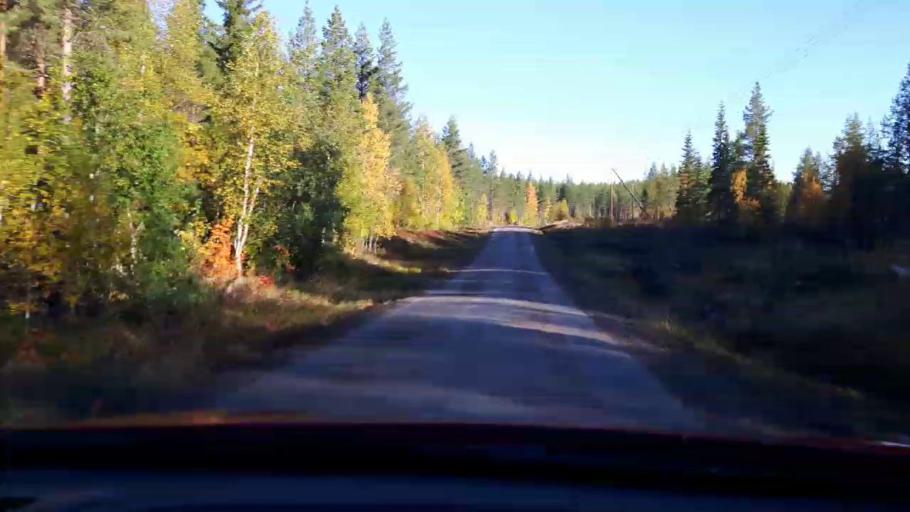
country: SE
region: Jaemtland
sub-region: Stroemsunds Kommun
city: Stroemsund
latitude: 64.3788
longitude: 15.1492
